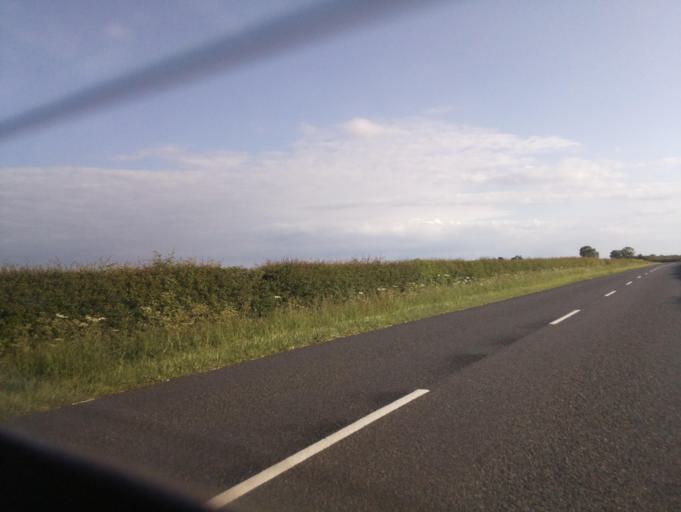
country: GB
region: England
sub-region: Lincolnshire
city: Navenby
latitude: 53.1060
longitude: -0.6055
